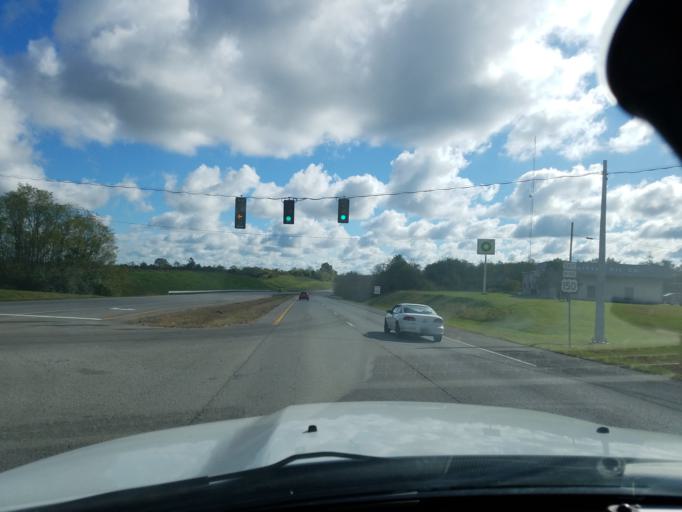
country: US
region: Kentucky
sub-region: Boyle County
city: Danville
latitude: 37.6208
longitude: -84.7531
